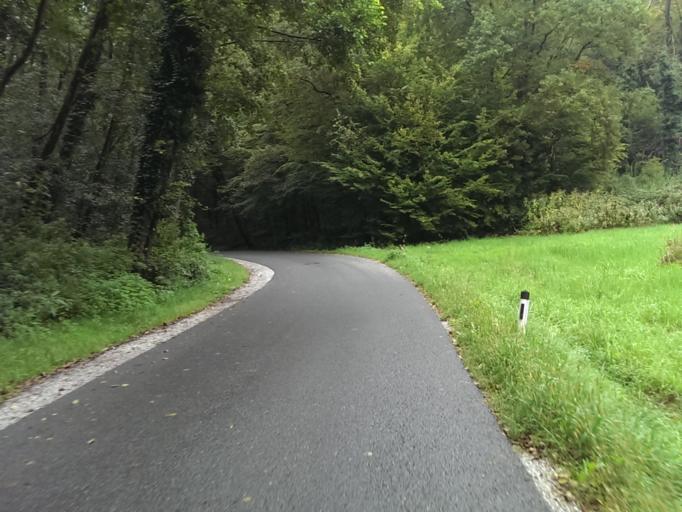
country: AT
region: Styria
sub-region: Politischer Bezirk Graz-Umgebung
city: Hart bei Graz
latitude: 47.0644
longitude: 15.4991
